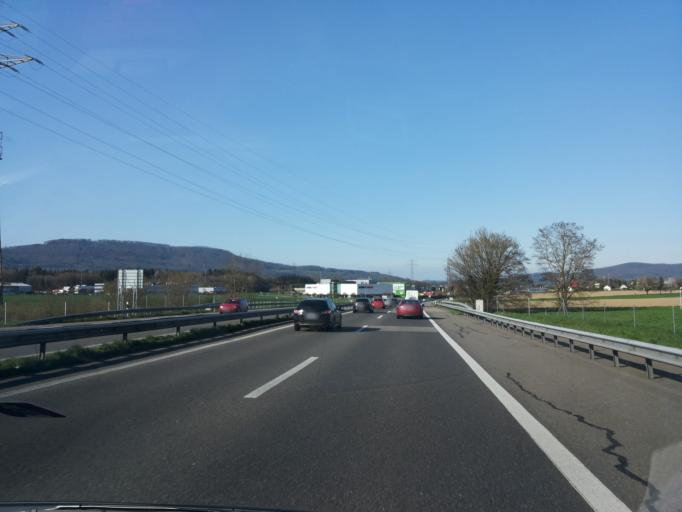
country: CH
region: Aargau
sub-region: Bezirk Aarau
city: Graenichen
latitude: 47.3817
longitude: 8.1108
